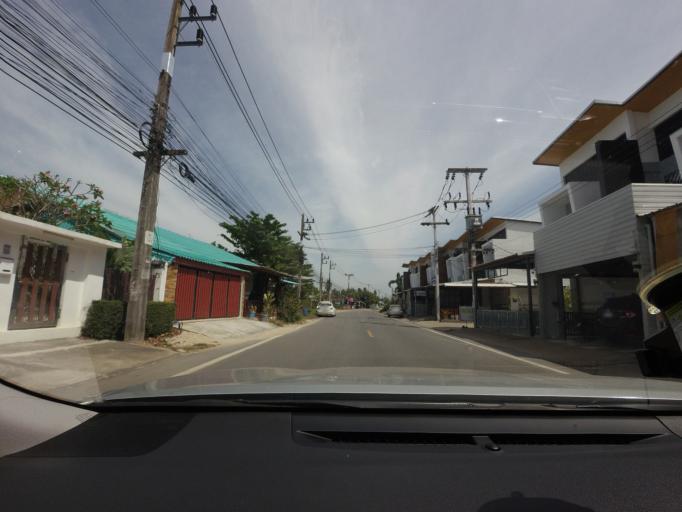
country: TH
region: Narathiwat
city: Narathiwat
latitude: 6.4273
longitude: 101.8112
